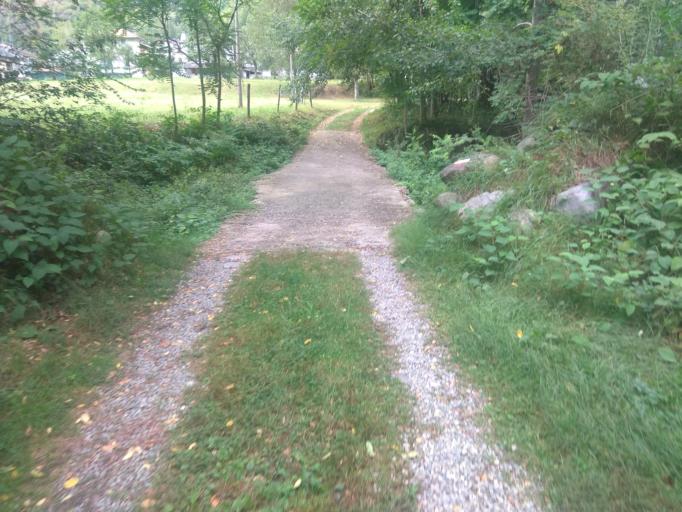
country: IT
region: Piedmont
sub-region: Provincia di Vercelli
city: Vocca
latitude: 45.8250
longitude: 8.1710
